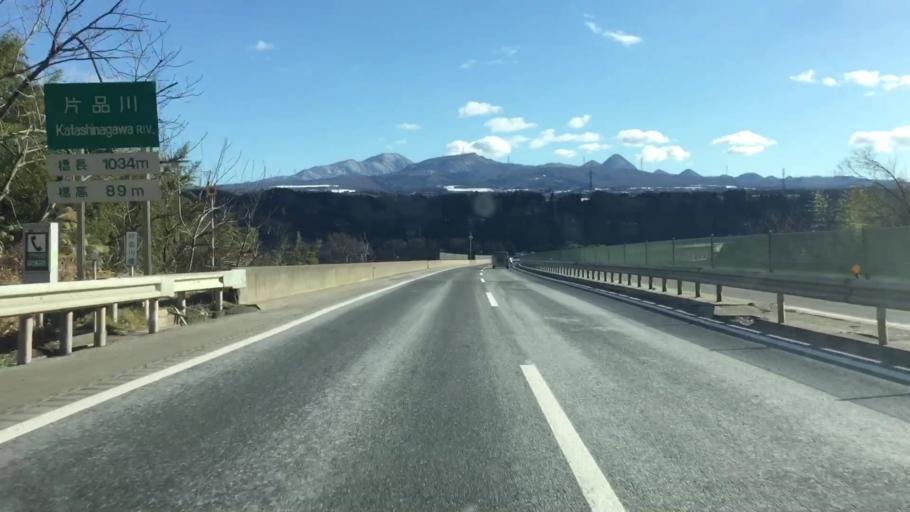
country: JP
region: Gunma
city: Numata
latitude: 36.6529
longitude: 139.0740
